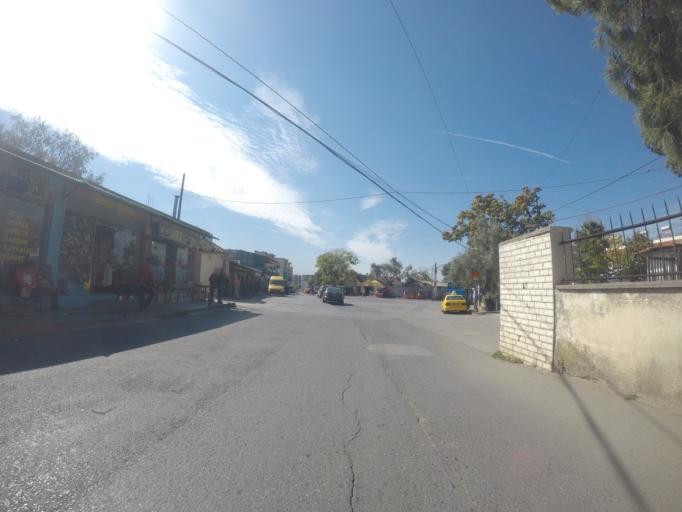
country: AL
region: Tirane
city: Tirana
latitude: 41.3453
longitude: 19.8511
